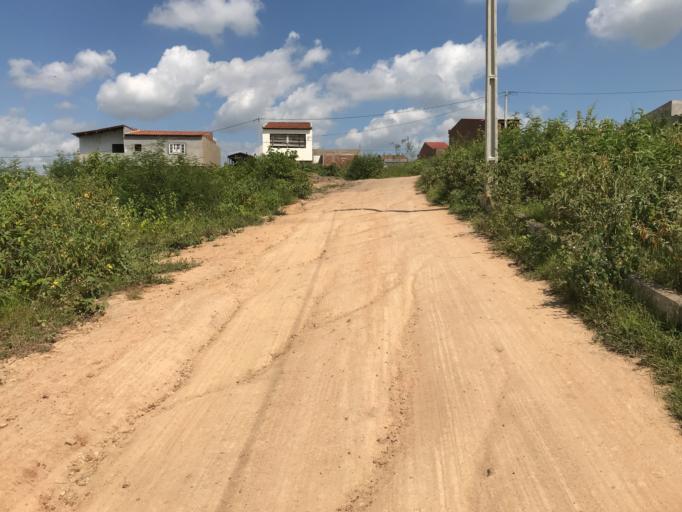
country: BR
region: Pernambuco
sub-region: Bezerros
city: Bezerros
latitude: -8.2260
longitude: -35.7533
